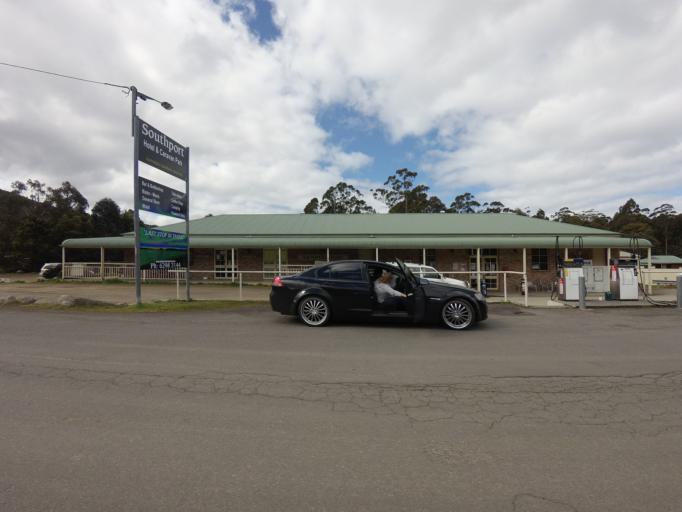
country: AU
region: Tasmania
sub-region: Huon Valley
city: Geeveston
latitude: -43.4241
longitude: 146.9726
